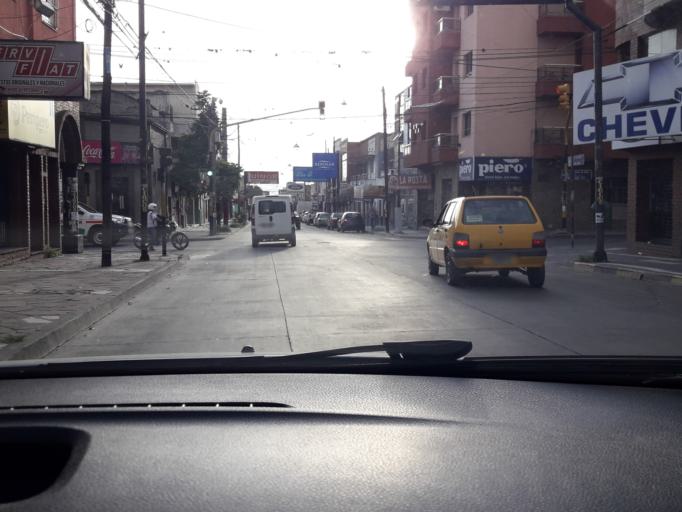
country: AR
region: Jujuy
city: San Salvador de Jujuy
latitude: -24.1913
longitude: -65.2991
